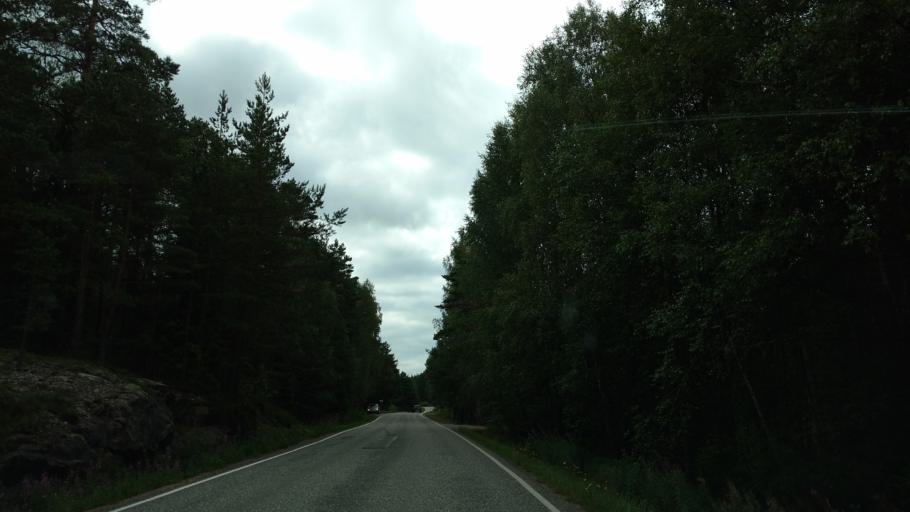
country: FI
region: Varsinais-Suomi
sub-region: Aboland-Turunmaa
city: Dragsfjaerd
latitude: 60.0254
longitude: 22.4594
